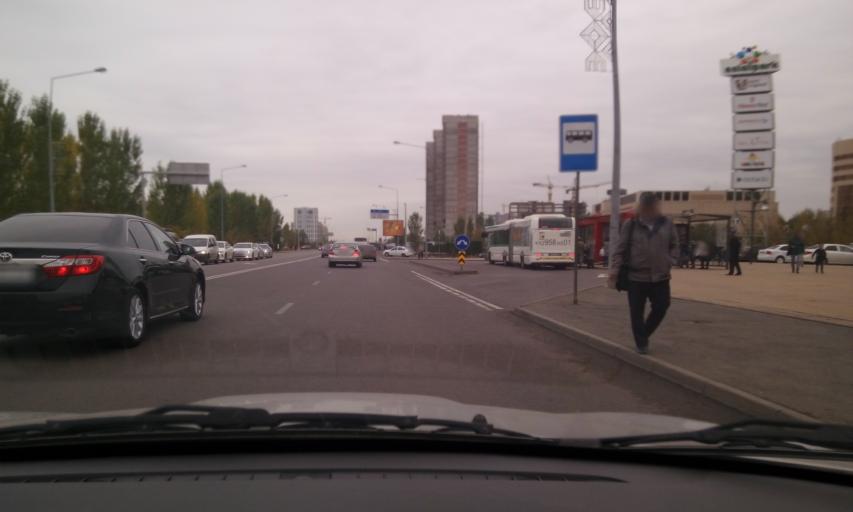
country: KZ
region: Astana Qalasy
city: Astana
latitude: 51.1281
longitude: 71.4134
